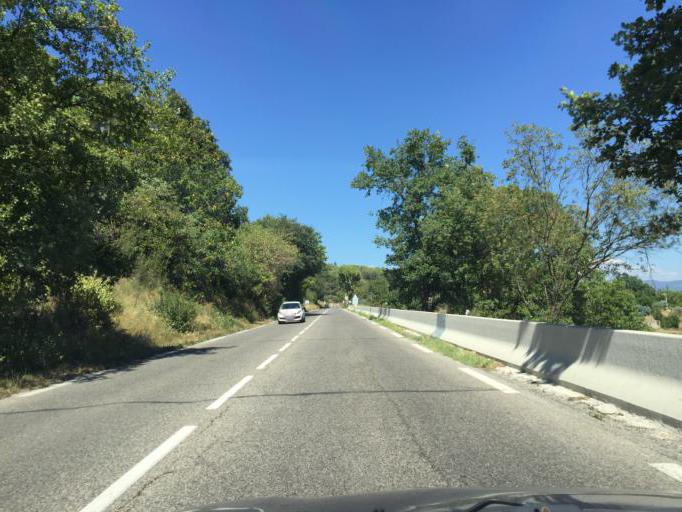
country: FR
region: Provence-Alpes-Cote d'Azur
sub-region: Departement des Alpes-de-Haute-Provence
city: Peyruis
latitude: 44.0206
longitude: 5.9297
